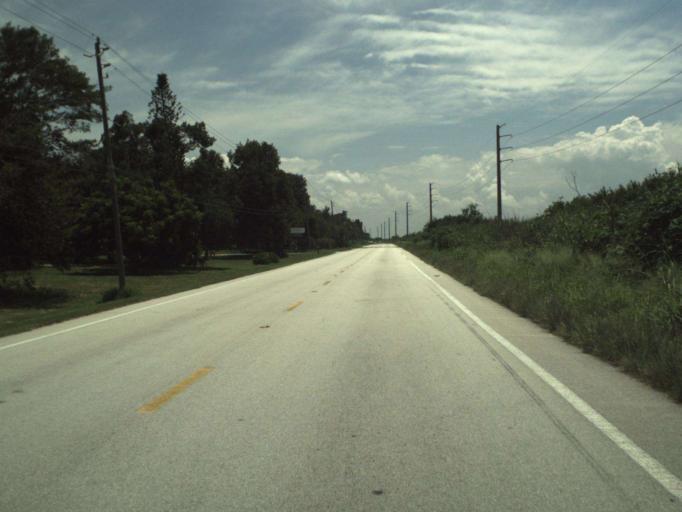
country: US
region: Florida
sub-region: Palm Beach County
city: Pahokee
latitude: 26.9319
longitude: -80.6115
